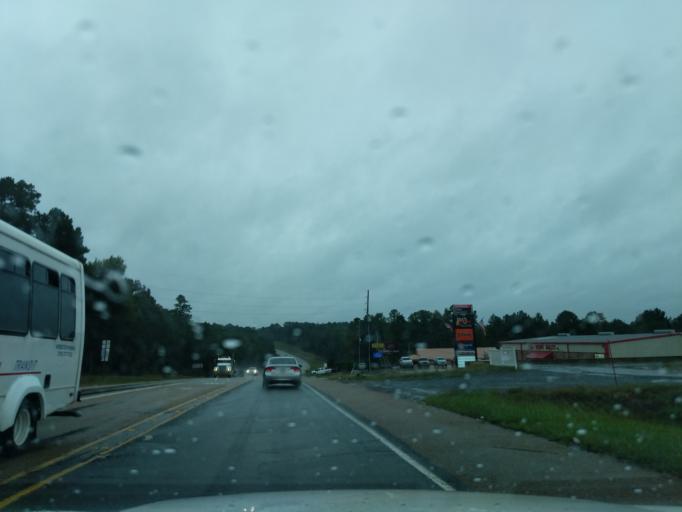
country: US
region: Louisiana
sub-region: Webster Parish
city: Minden
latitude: 32.6017
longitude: -93.2500
